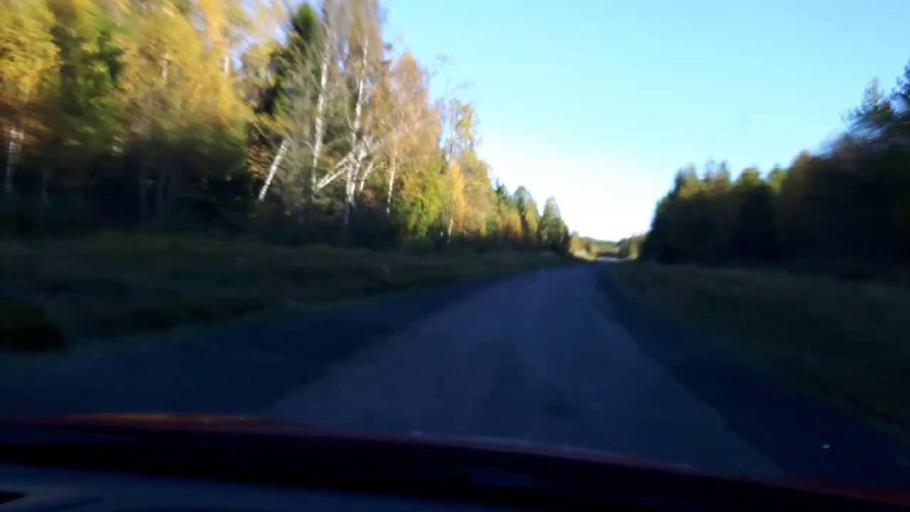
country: SE
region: Jaemtland
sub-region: OEstersunds Kommun
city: Lit
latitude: 63.5940
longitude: 14.8361
